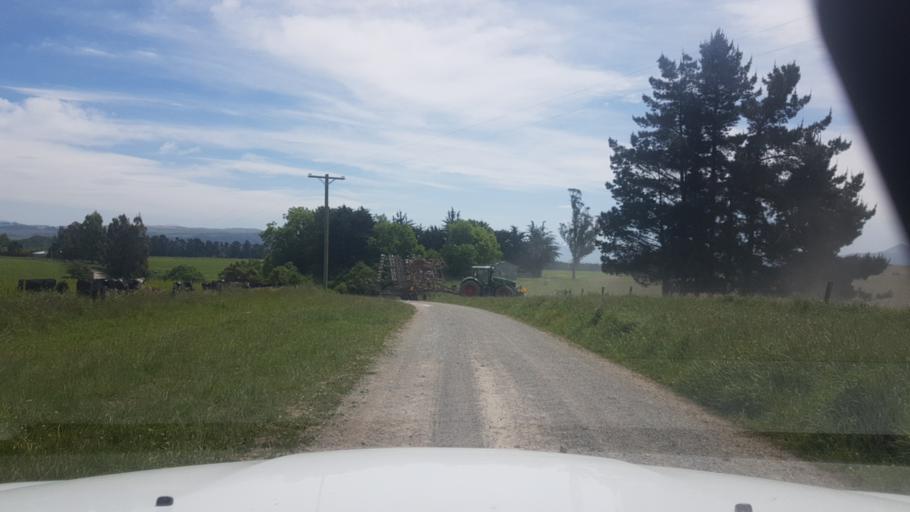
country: NZ
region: Canterbury
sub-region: Timaru District
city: Pleasant Point
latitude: -44.1675
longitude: 171.0148
